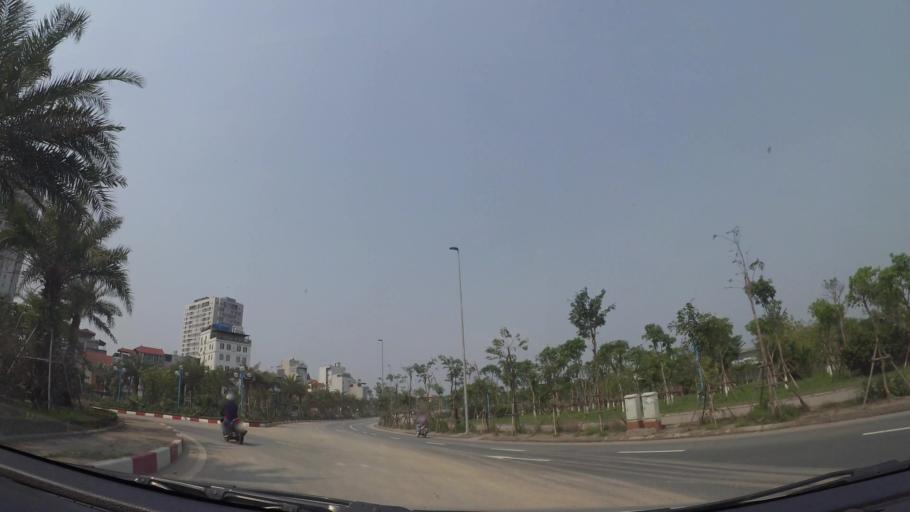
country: VN
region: Ha Noi
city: Tay Ho
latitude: 21.0840
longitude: 105.8138
